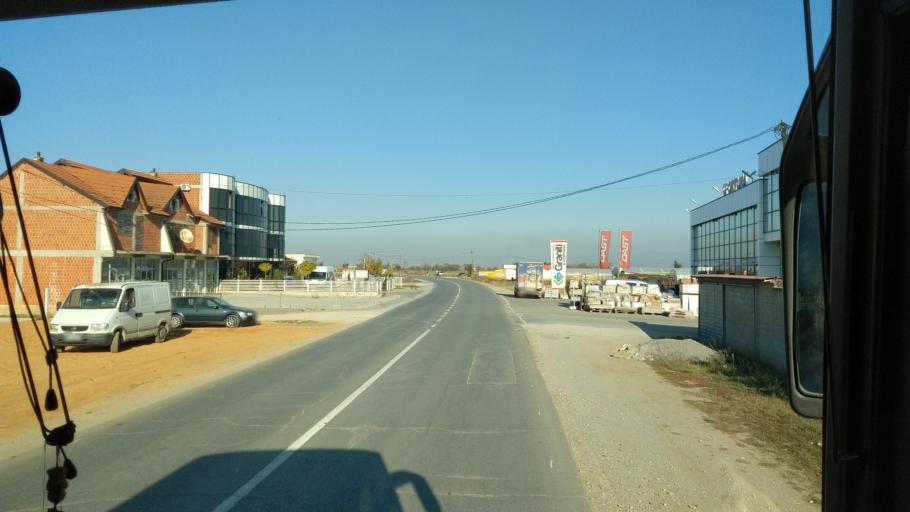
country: XK
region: Ferizaj
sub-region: Komuna e Shtimes
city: Shtime
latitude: 42.4506
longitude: 21.0680
